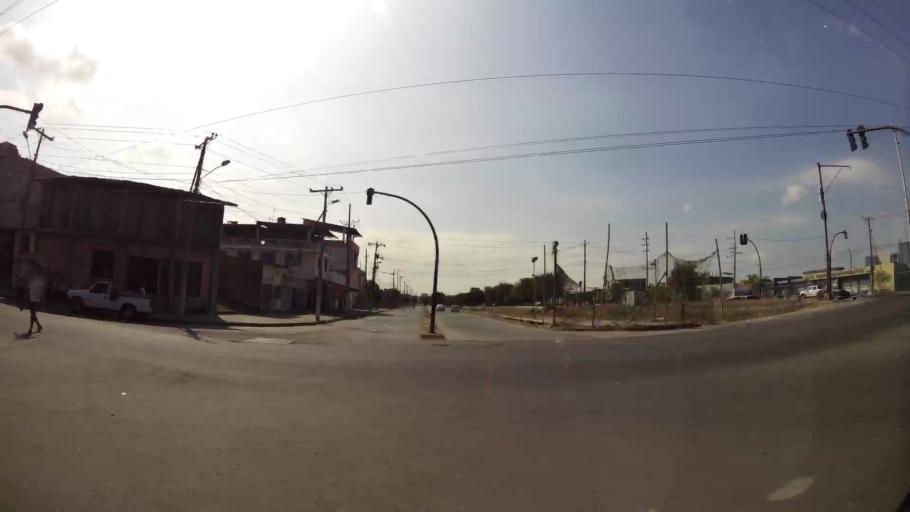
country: EC
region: Guayas
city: Eloy Alfaro
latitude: -2.1708
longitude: -79.8062
